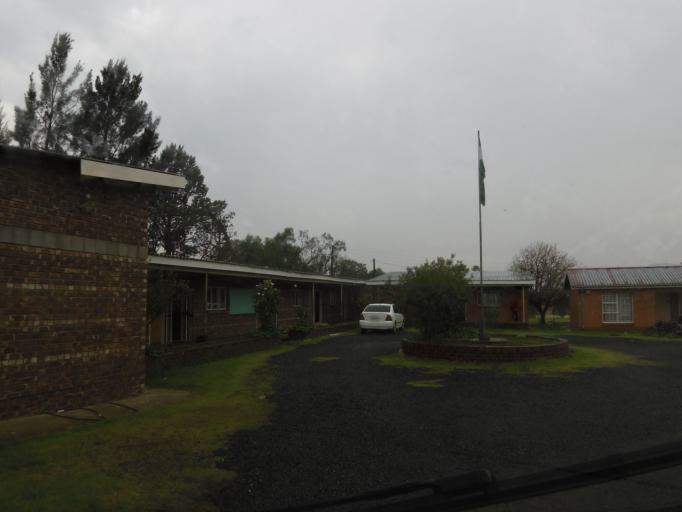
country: LS
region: Mafeteng
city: Mafeteng
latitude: -29.8184
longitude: 27.2389
